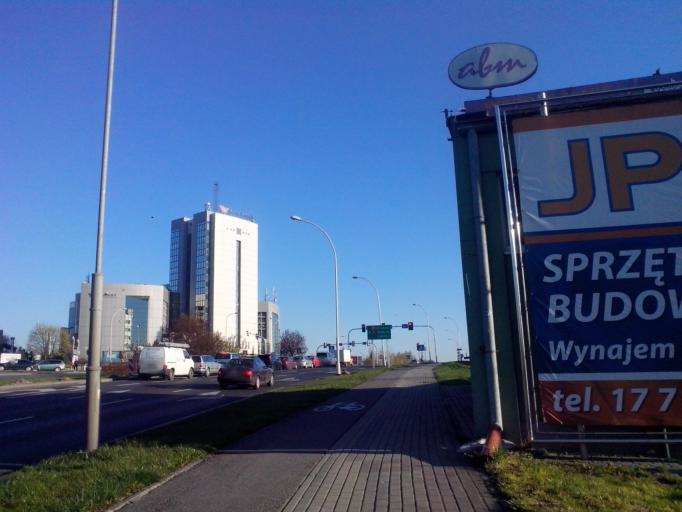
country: PL
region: Subcarpathian Voivodeship
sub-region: Rzeszow
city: Rzeszow
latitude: 50.0262
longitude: 21.9770
